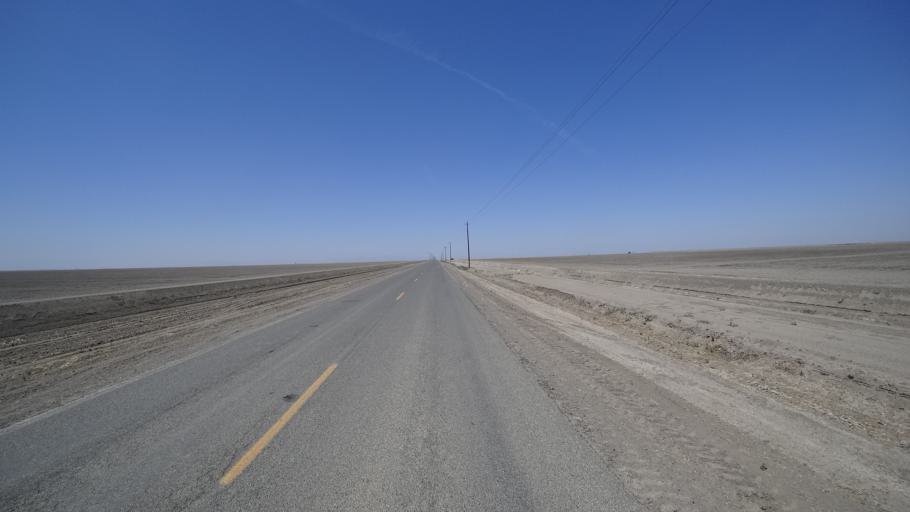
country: US
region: California
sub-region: Kings County
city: Corcoran
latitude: 36.0215
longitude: -119.6015
